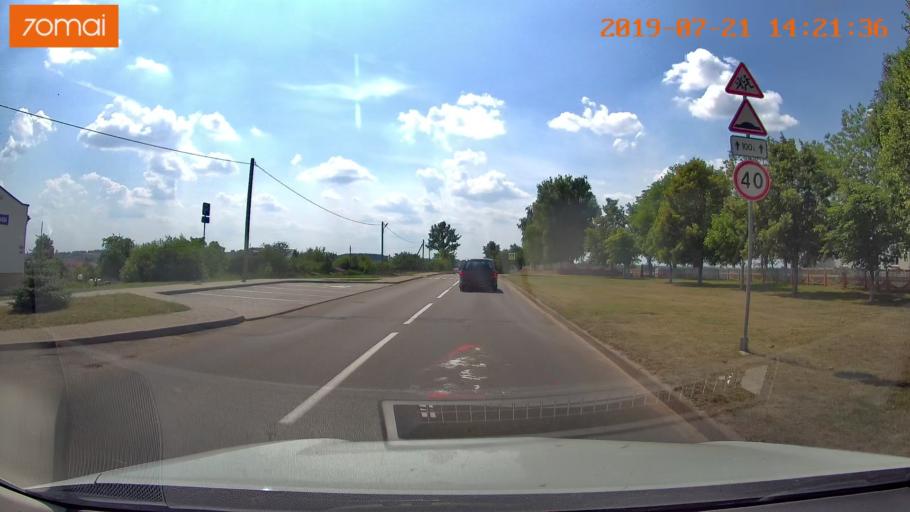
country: BY
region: Grodnenskaya
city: Karelichy
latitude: 53.5757
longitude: 26.1435
